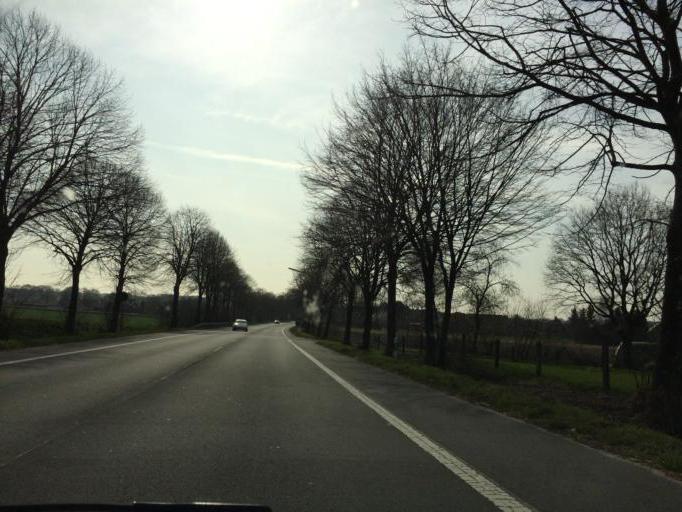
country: DE
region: North Rhine-Westphalia
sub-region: Regierungsbezirk Munster
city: Haltern
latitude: 51.7805
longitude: 7.1699
